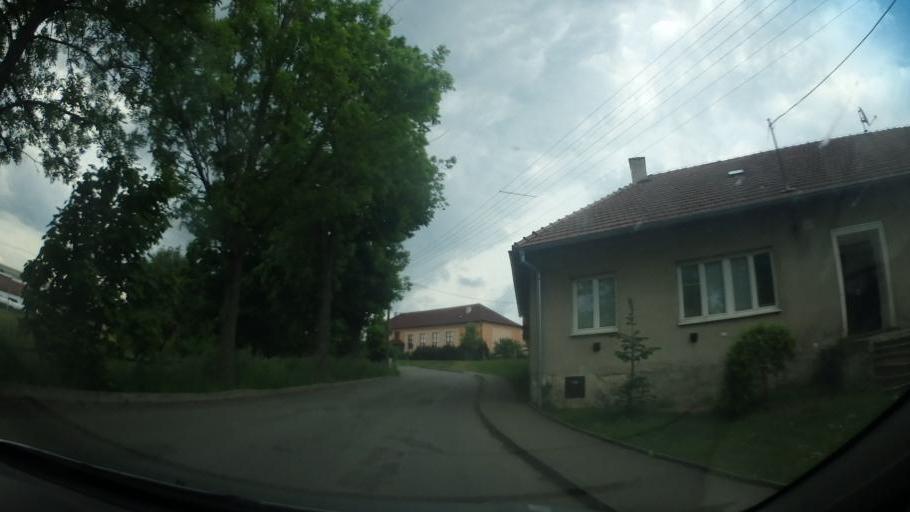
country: CZ
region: South Moravian
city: Olesnice
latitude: 49.4856
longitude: 16.4216
